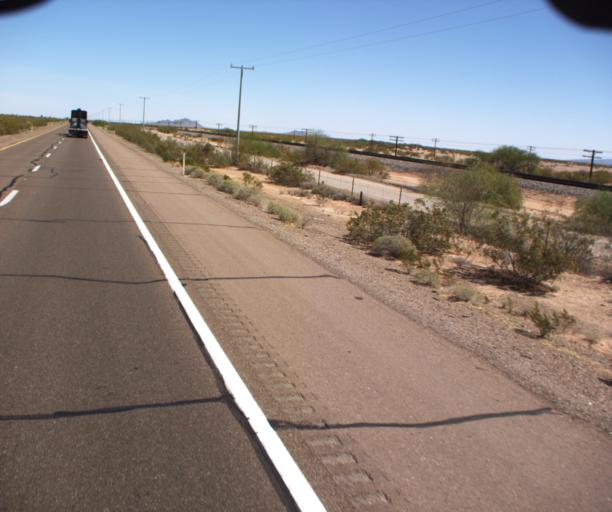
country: US
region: Arizona
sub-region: Yuma County
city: Wellton
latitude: 32.7620
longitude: -113.6311
